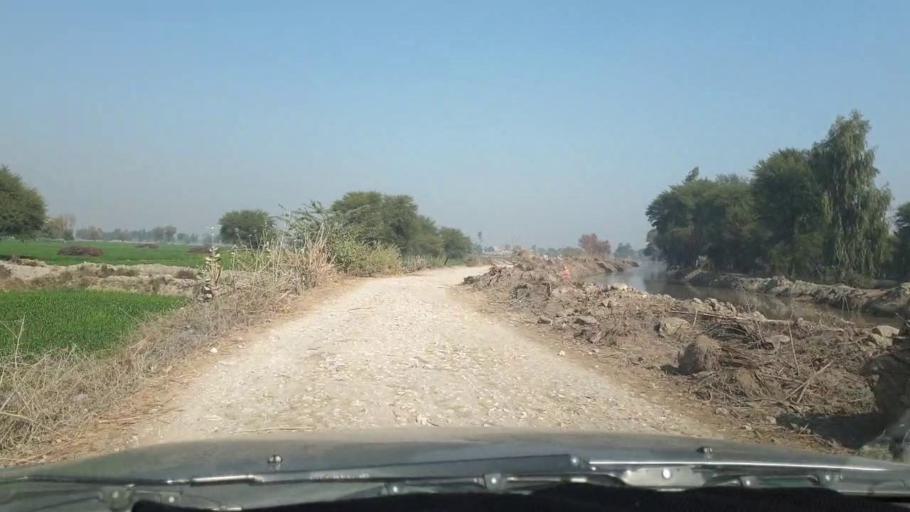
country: PK
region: Sindh
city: Khanpur
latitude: 27.7996
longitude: 69.5690
